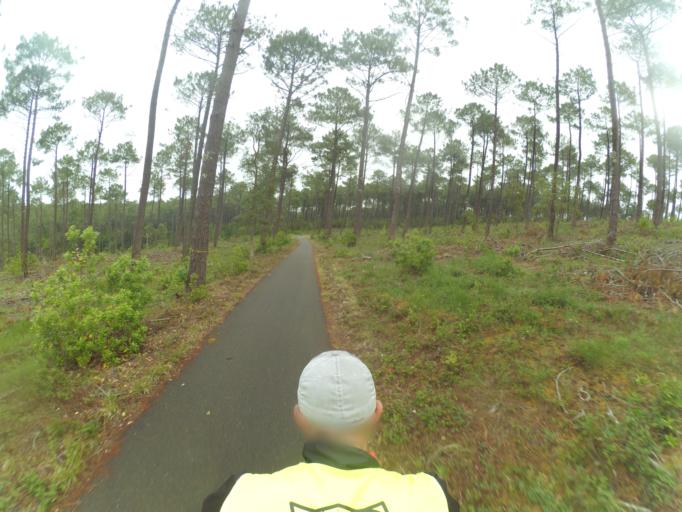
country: FR
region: Aquitaine
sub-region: Departement des Landes
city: Mimizan
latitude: 44.2201
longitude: -1.2509
